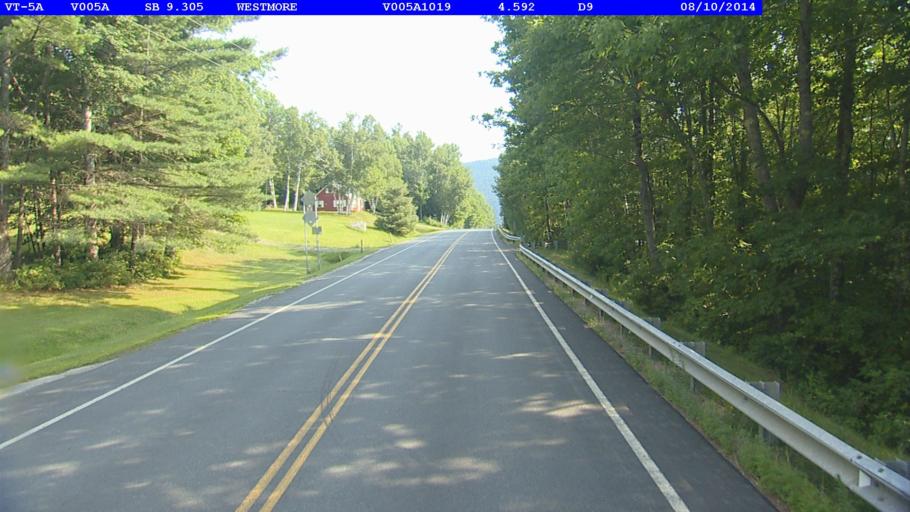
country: US
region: Vermont
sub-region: Caledonia County
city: Lyndonville
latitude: 44.7566
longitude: -72.0523
